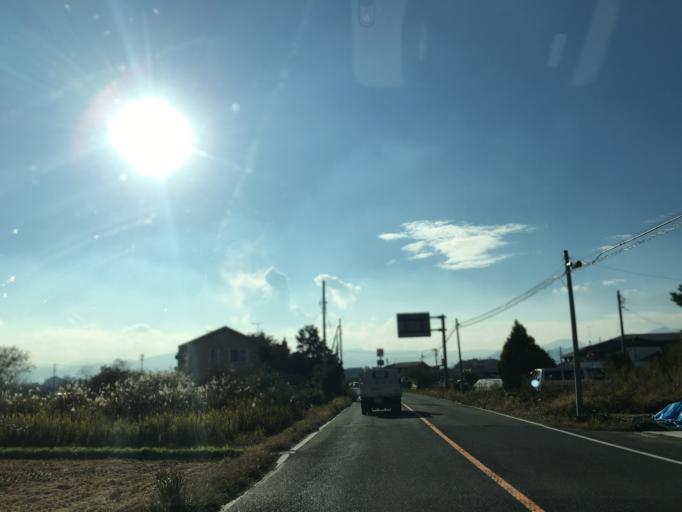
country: JP
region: Fukushima
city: Koriyama
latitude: 37.4204
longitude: 140.3134
